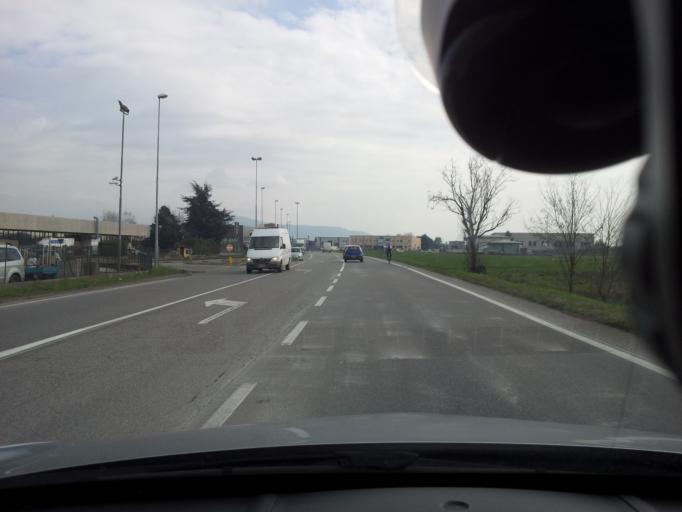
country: IT
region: Lombardy
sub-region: Provincia di Bergamo
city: Grumello del Monte
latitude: 45.6295
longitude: 9.8760
